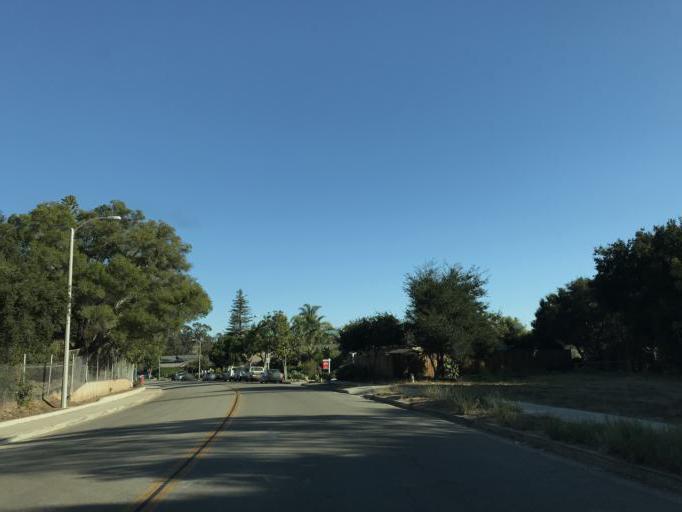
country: US
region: California
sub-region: Santa Barbara County
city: Goleta
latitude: 34.4584
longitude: -119.8145
